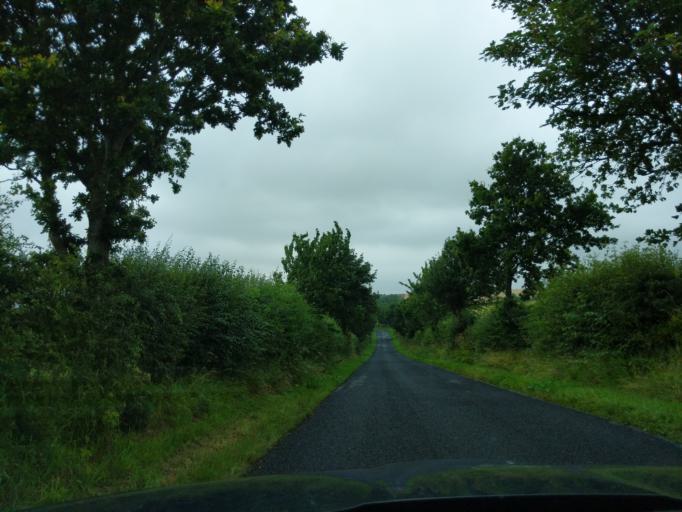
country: GB
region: England
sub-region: Northumberland
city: Ford
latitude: 55.7009
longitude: -2.1439
